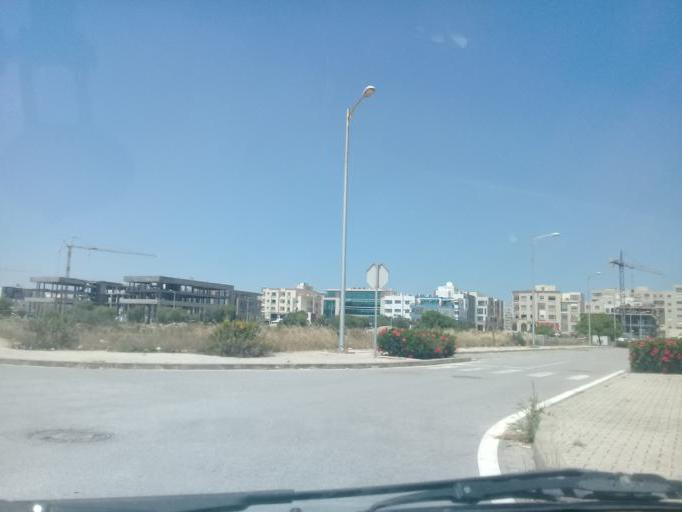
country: TN
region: Tunis
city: La Goulette
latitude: 36.8415
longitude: 10.2811
